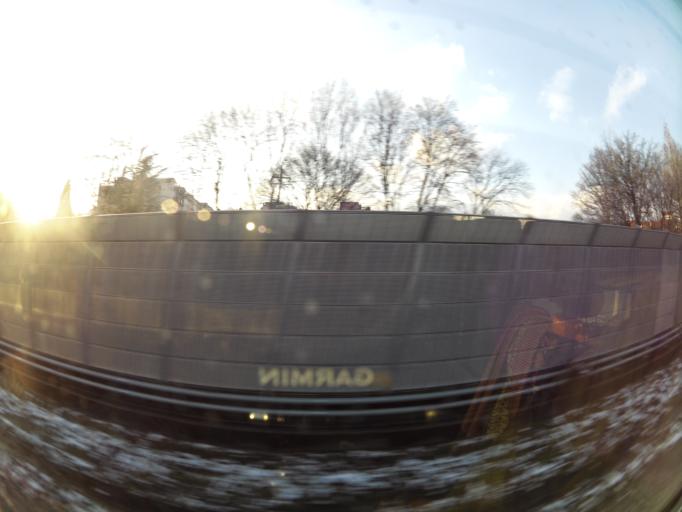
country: KR
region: Daejeon
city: Daejeon
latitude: 36.3656
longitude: 127.4196
